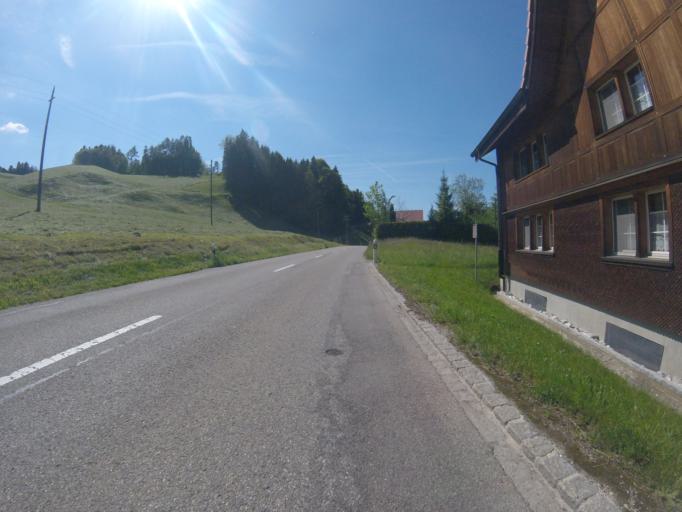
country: CH
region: Saint Gallen
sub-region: Wahlkreis Toggenburg
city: Oberhelfenschwil
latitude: 47.3770
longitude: 9.1172
